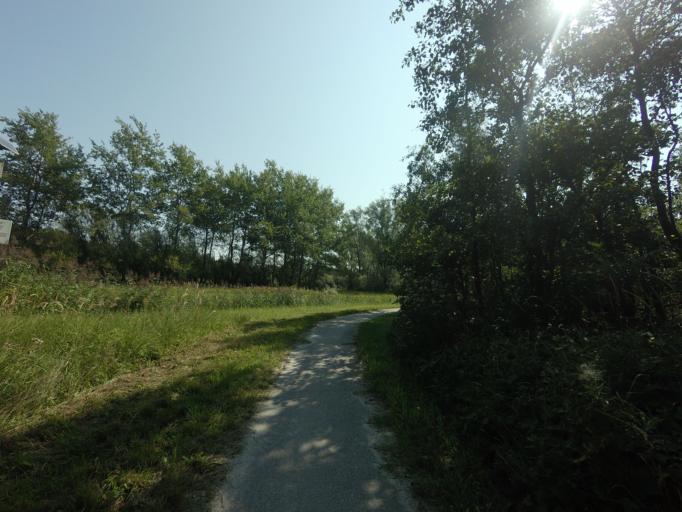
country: NL
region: Groningen
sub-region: Gemeente De Marne
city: Ulrum
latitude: 53.3922
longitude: 6.2560
